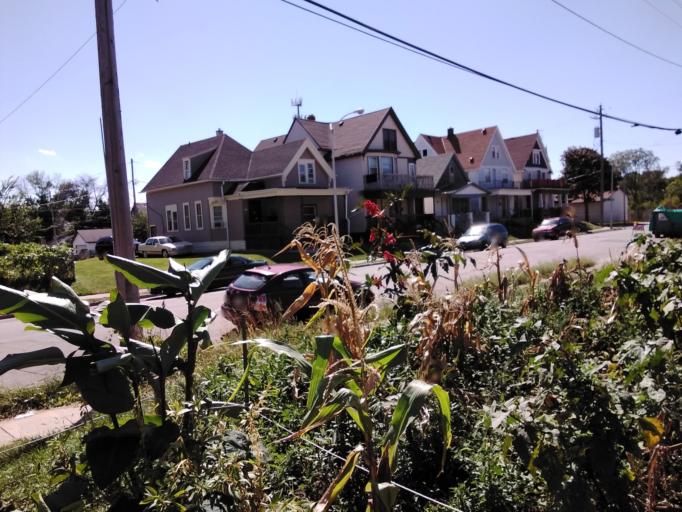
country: US
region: Wisconsin
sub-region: Milwaukee County
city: Milwaukee
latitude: 43.0529
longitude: -87.9503
